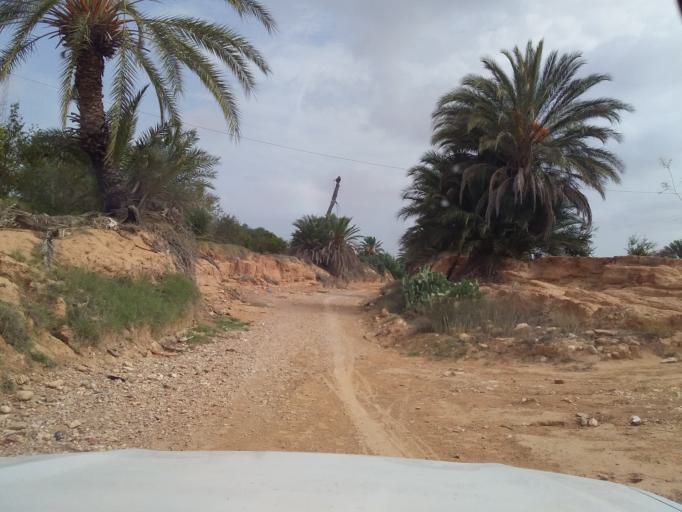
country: TN
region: Qabis
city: Gabes
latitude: 33.6297
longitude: 10.2992
